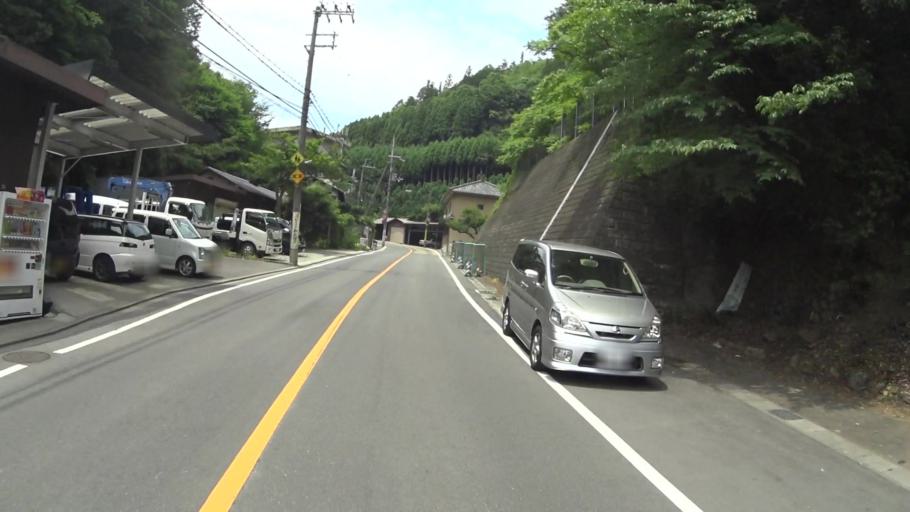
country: JP
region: Kyoto
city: Kyoto
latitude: 35.0459
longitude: 135.6836
